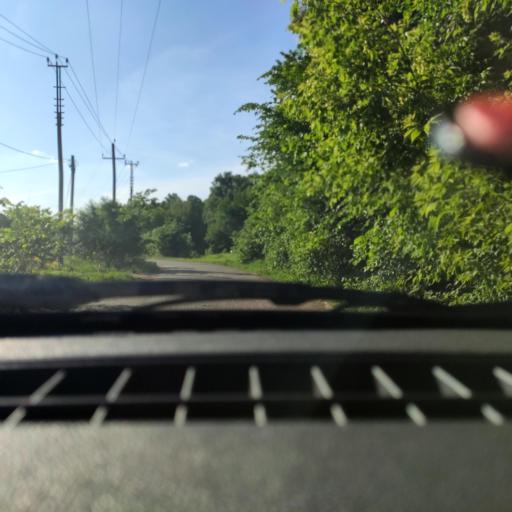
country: RU
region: Bashkortostan
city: Avdon
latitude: 54.4642
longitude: 55.8356
